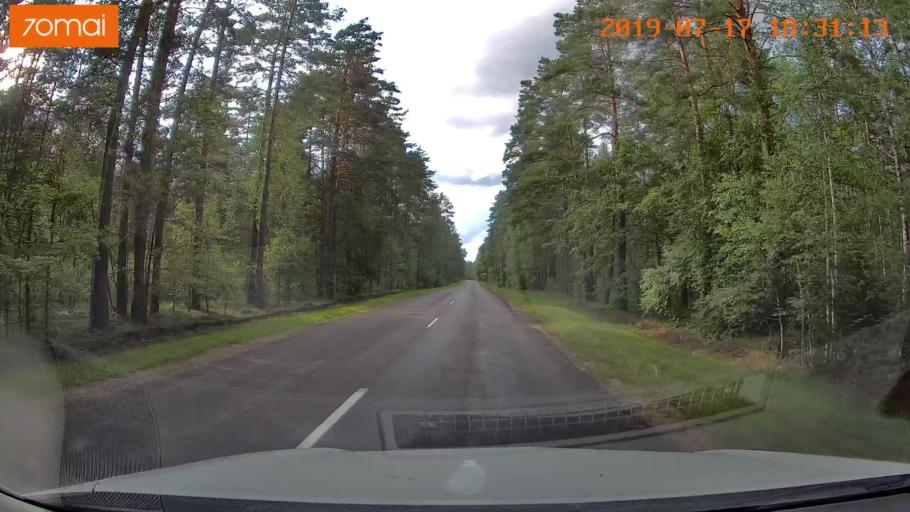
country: BY
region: Mogilev
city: Asipovichy
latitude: 53.2566
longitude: 28.6843
